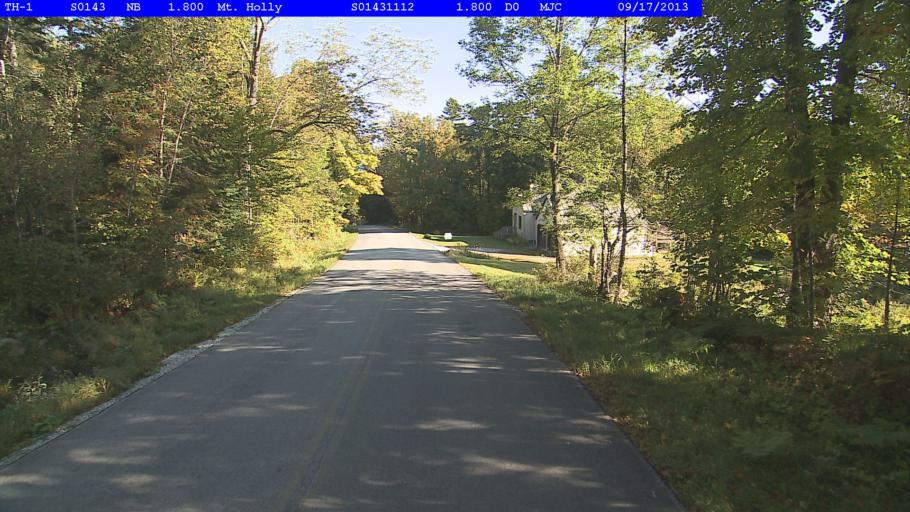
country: US
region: Vermont
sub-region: Rutland County
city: Rutland
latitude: 43.4250
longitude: -72.8194
